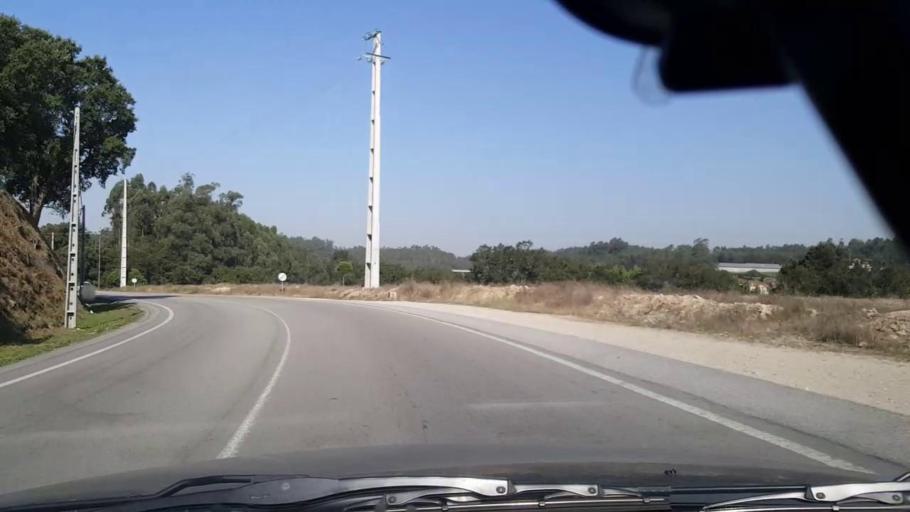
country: PT
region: Porto
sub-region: Vila do Conde
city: Arvore
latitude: 41.3486
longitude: -8.6788
